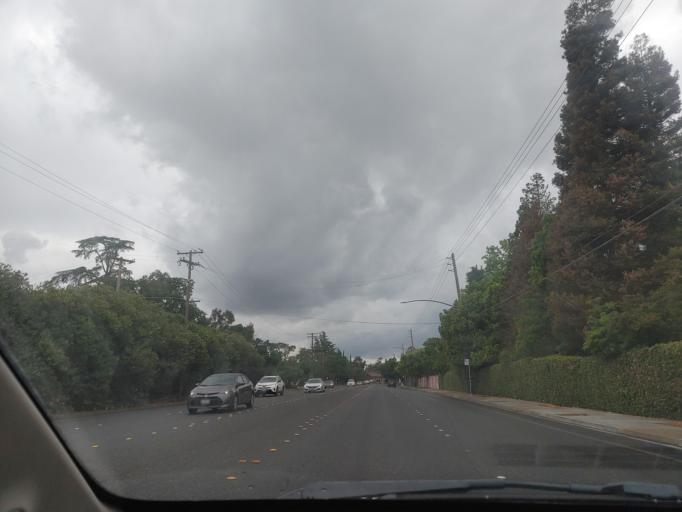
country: US
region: California
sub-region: Stanislaus County
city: Bystrom
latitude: 37.6526
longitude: -120.9503
